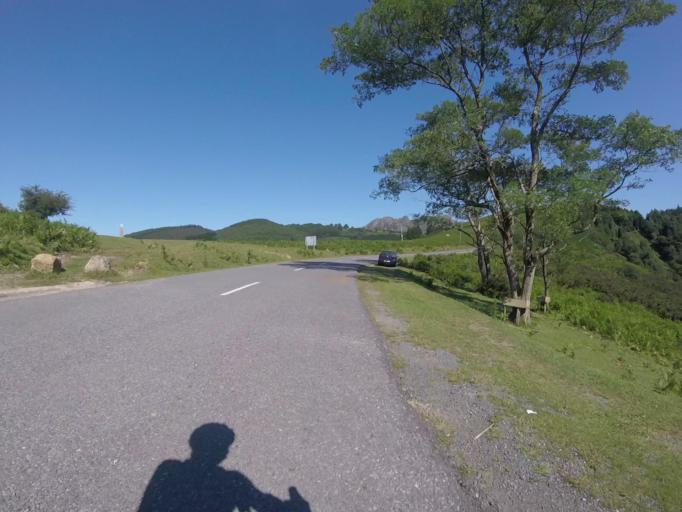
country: ES
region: Basque Country
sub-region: Provincia de Guipuzcoa
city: Irun
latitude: 43.2976
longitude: -1.8180
